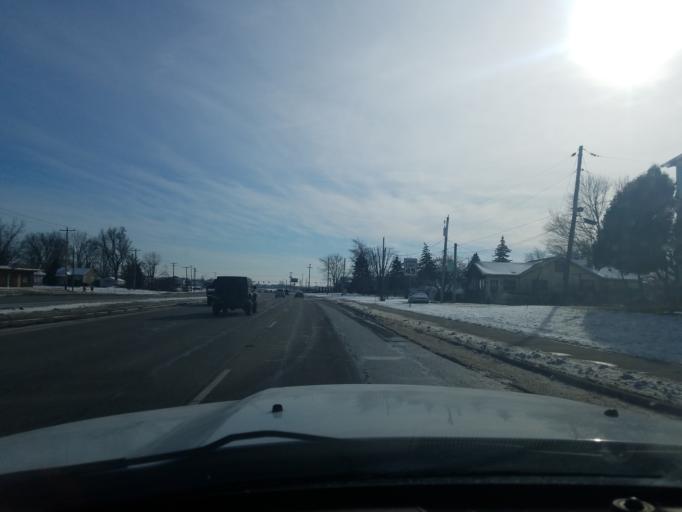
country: US
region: Indiana
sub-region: Allen County
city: Fort Wayne
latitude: 41.1501
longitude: -85.1653
